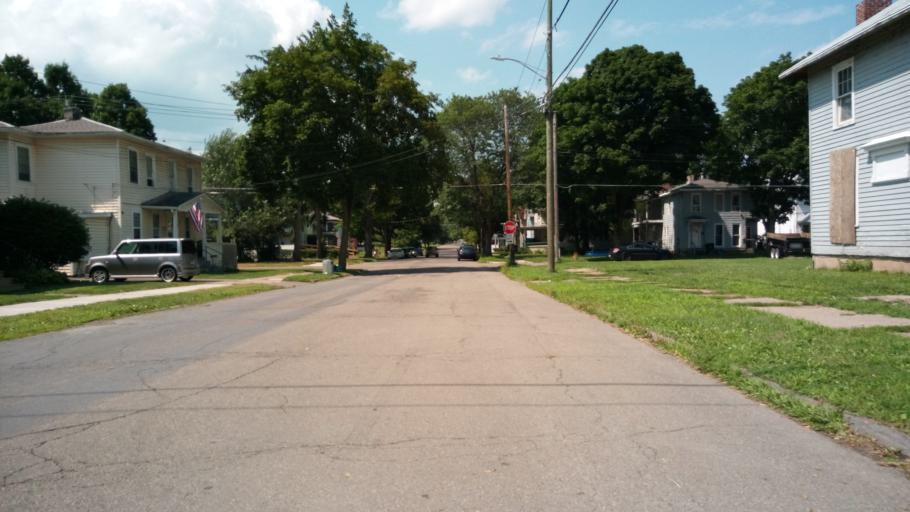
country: US
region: New York
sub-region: Chemung County
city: Elmira
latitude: 42.0868
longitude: -76.8200
